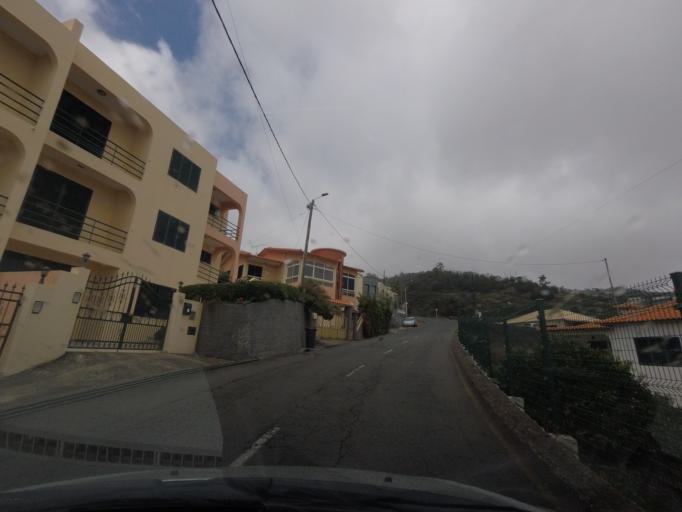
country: PT
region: Madeira
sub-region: Machico
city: Machico
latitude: 32.7049
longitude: -16.7766
